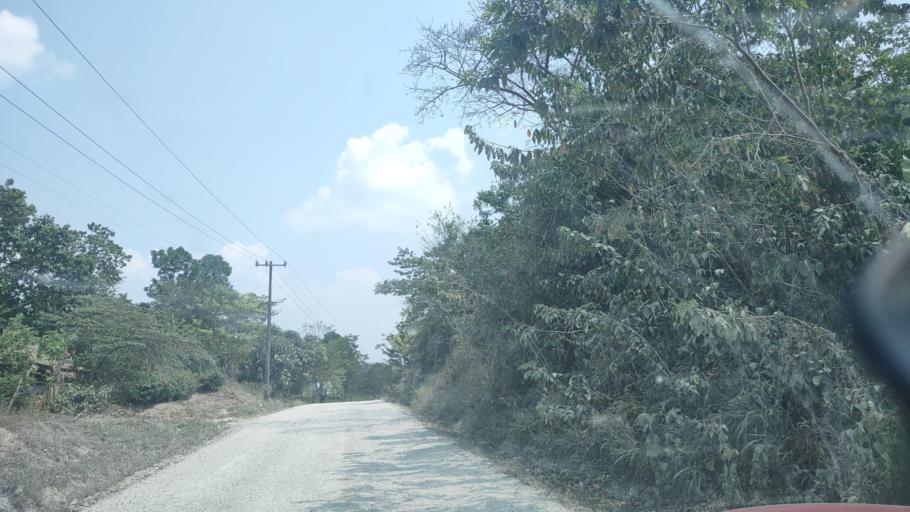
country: MX
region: Tabasco
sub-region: Huimanguillo
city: Francisco Rueda
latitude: 17.5895
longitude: -93.8927
